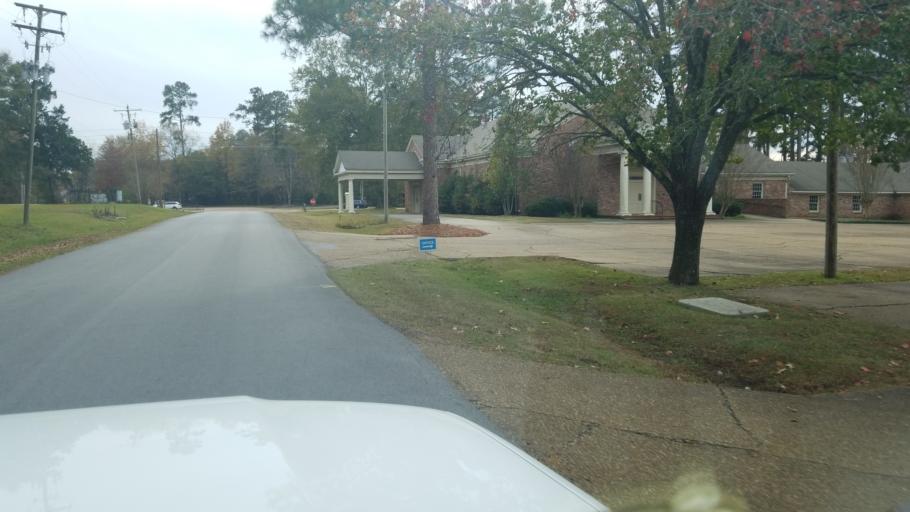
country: US
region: Mississippi
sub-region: Madison County
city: Ridgeland
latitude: 32.3800
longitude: -90.0323
